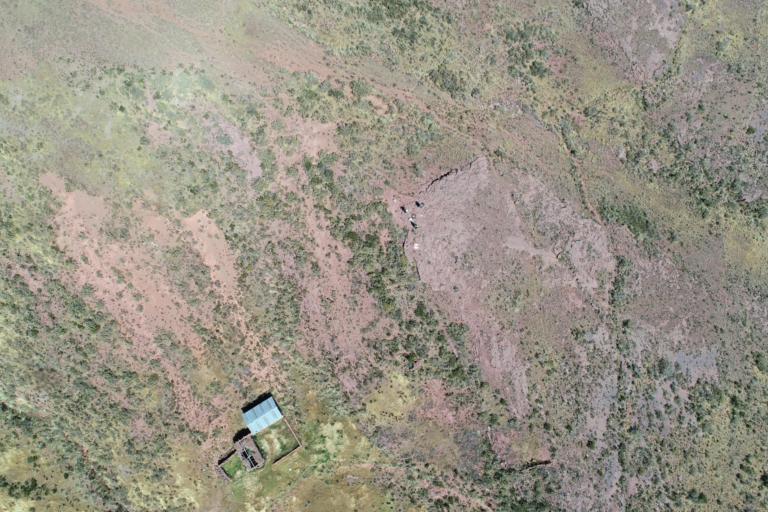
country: BO
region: La Paz
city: Tiahuanaco
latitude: -16.6096
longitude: -68.7606
